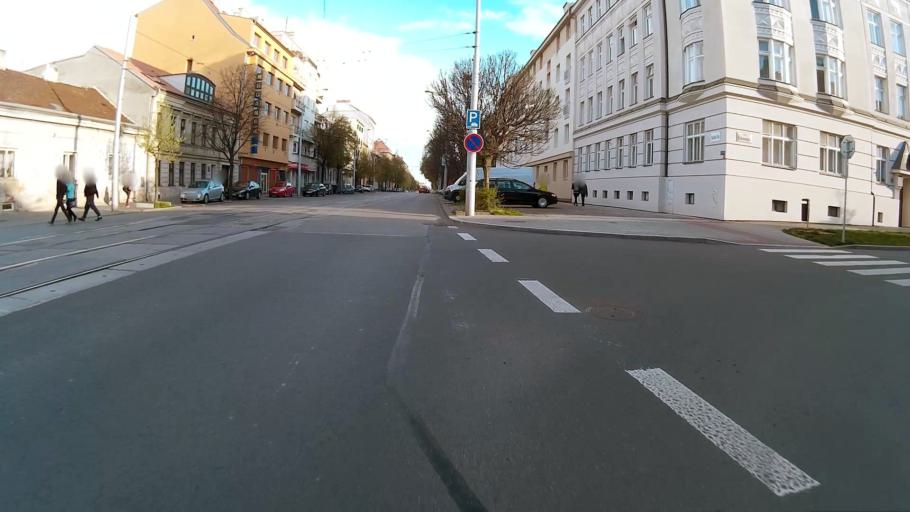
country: CZ
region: South Moravian
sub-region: Mesto Brno
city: Brno
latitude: 49.2203
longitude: 16.5969
